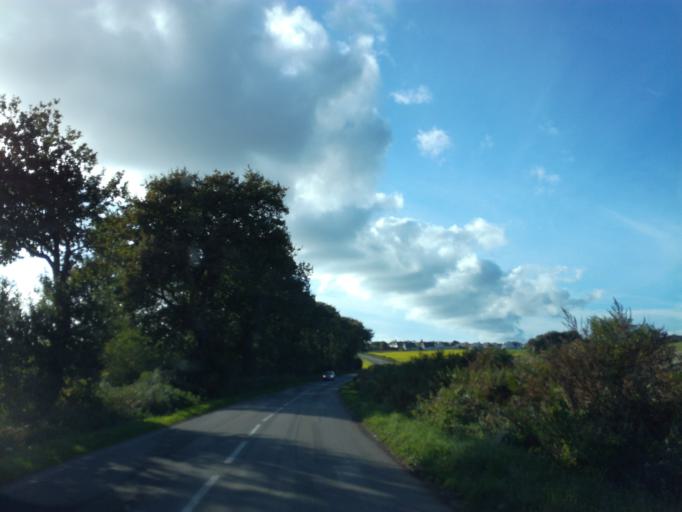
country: FR
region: Brittany
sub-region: Departement du Morbihan
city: Le Sourn
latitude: 48.0401
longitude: -2.9733
